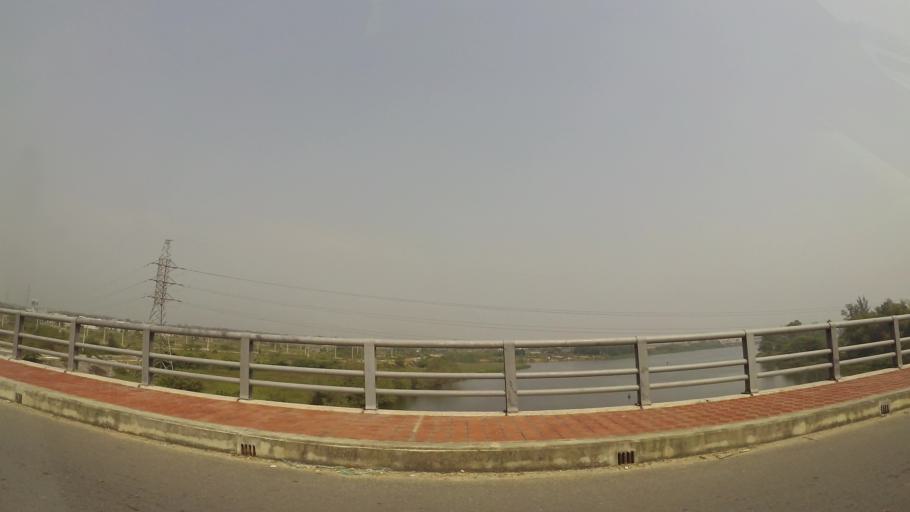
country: VN
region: Da Nang
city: Cam Le
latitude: 15.9688
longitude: 108.2165
